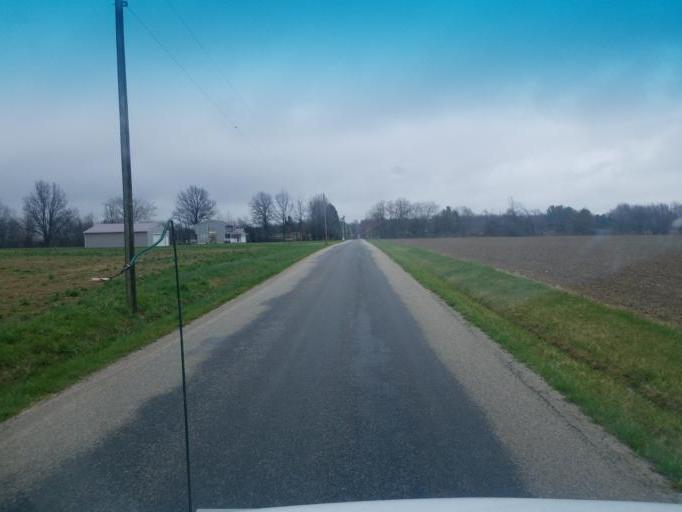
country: US
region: Ohio
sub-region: Huron County
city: Plymouth
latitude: 40.9594
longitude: -82.6850
